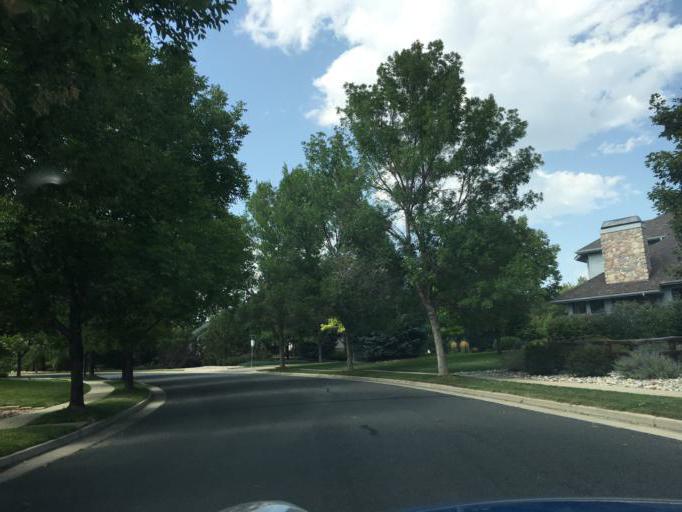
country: US
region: Colorado
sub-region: Boulder County
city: Lafayette
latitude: 40.0191
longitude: -105.1180
